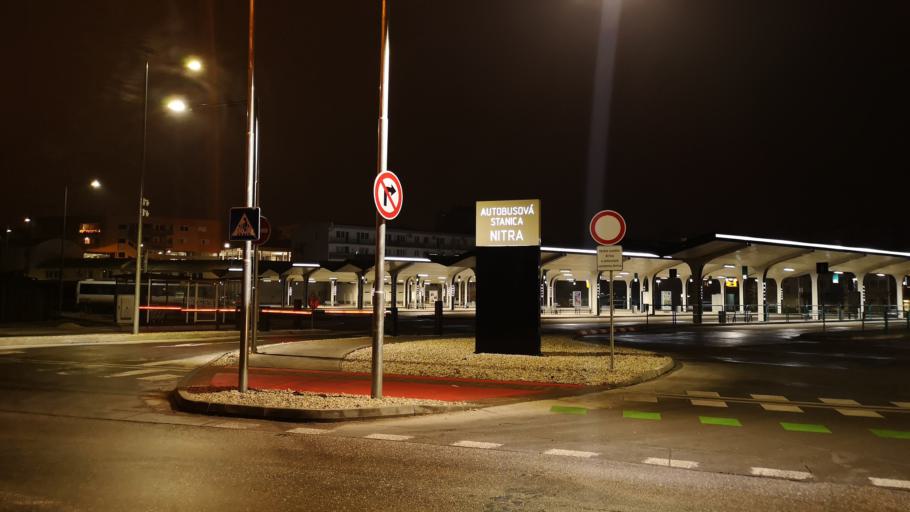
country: SK
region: Nitriansky
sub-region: Okres Nitra
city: Nitra
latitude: 48.3036
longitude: 18.0798
